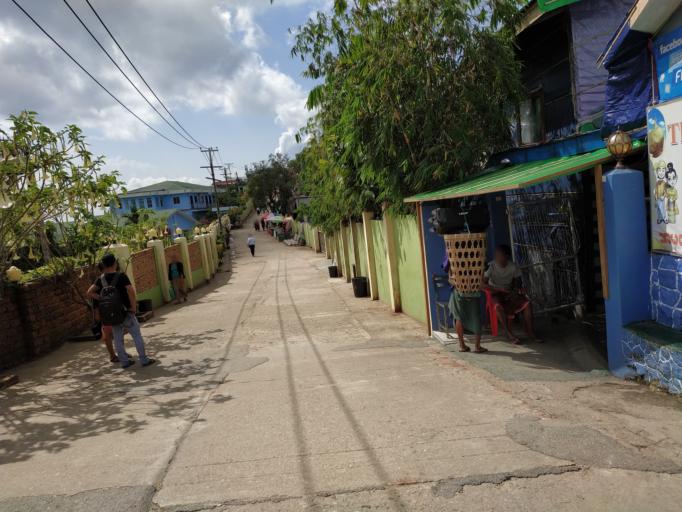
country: MM
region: Mon
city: Kyaikto
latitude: 17.4775
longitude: 97.1012
